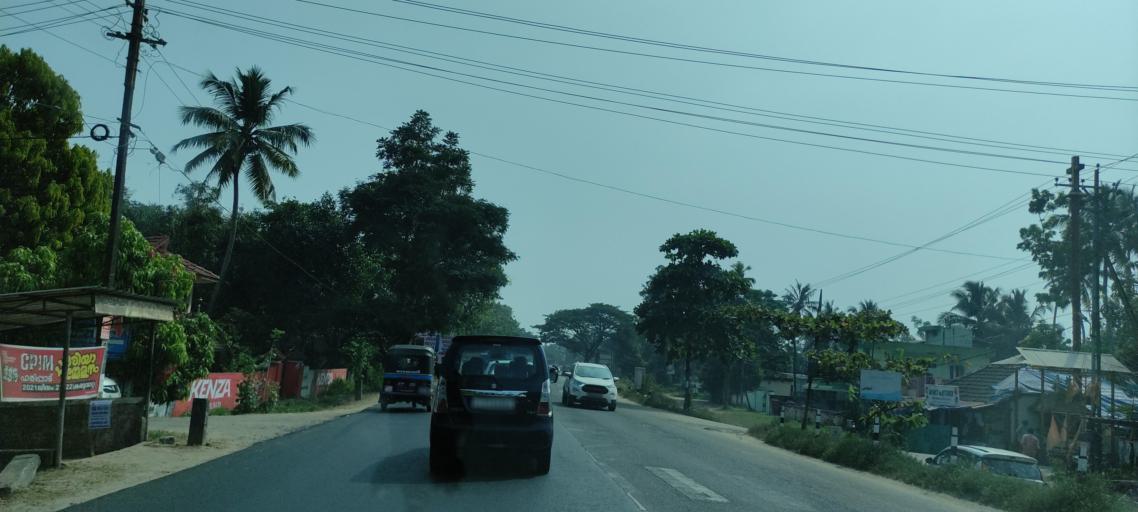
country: IN
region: Kerala
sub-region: Alappuzha
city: Mavelikara
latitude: 9.2689
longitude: 76.4609
